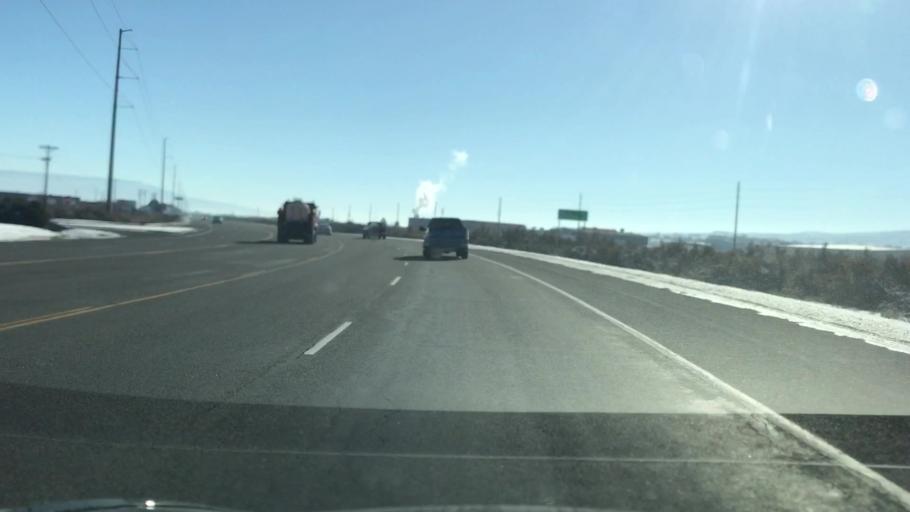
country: US
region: Colorado
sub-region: Mesa County
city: Redlands
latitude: 39.1086
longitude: -108.6417
